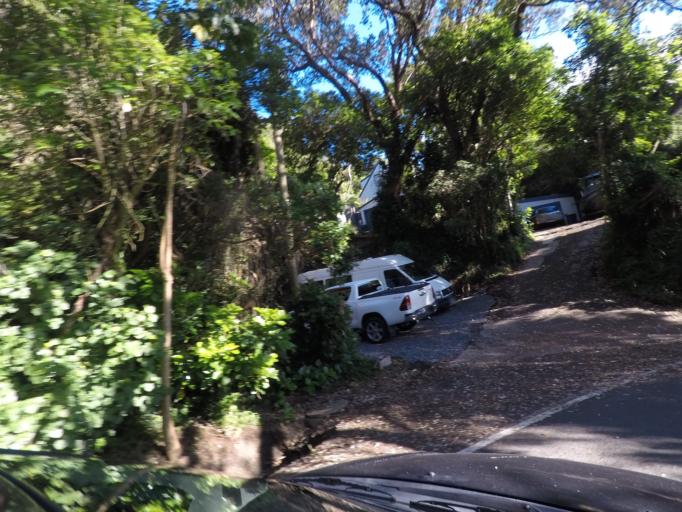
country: NZ
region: Auckland
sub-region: Auckland
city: Titirangi
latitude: -37.0140
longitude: 174.6032
